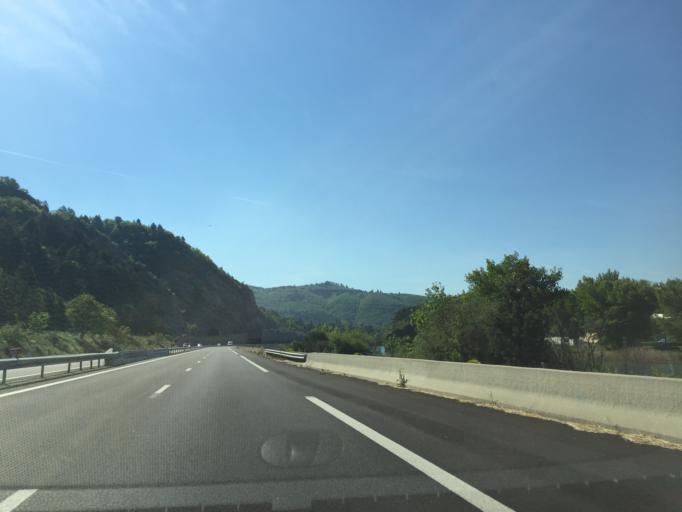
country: FR
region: Provence-Alpes-Cote d'Azur
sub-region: Departement des Alpes-de-Haute-Provence
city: Sisteron
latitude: 44.1958
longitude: 5.9504
